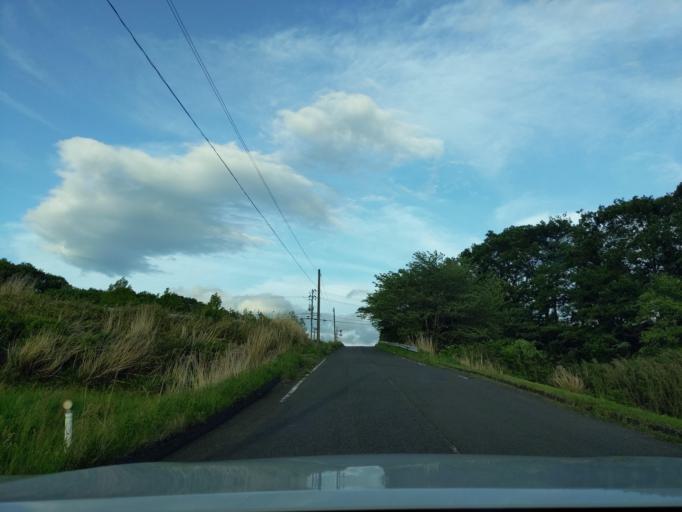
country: JP
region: Fukushima
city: Miharu
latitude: 37.4119
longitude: 140.4701
